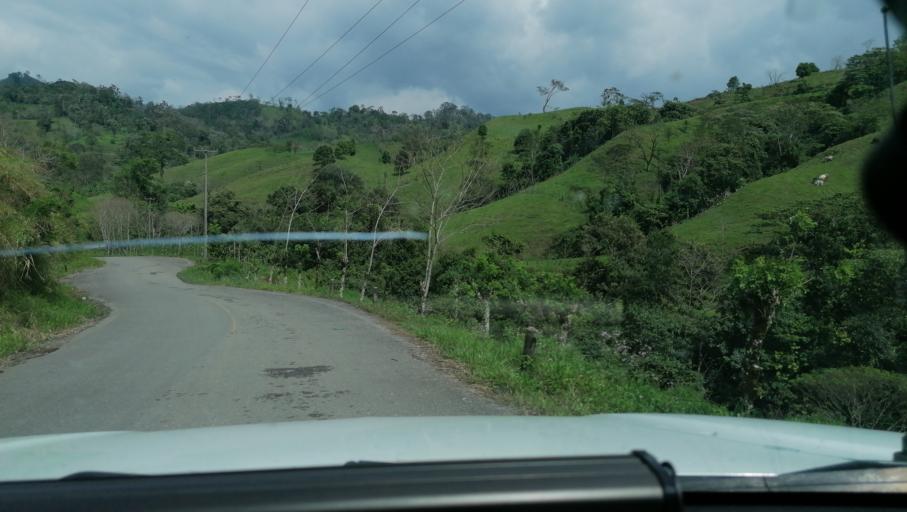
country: MX
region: Chiapas
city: Ocotepec
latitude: 17.3143
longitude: -93.1711
